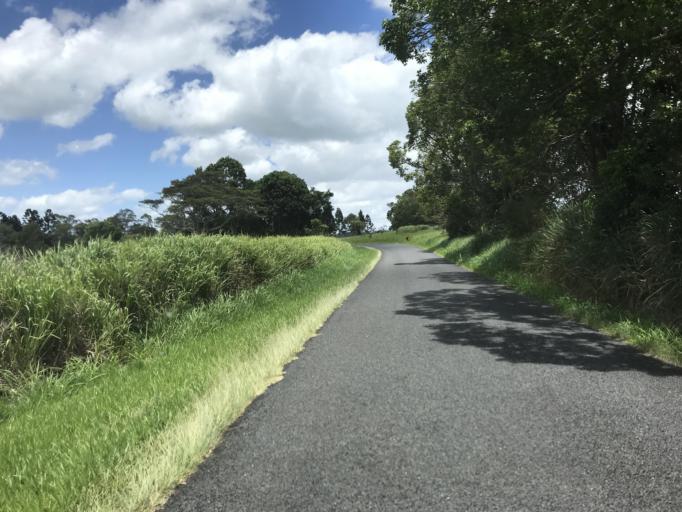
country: AU
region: Queensland
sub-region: Tablelands
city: Atherton
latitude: -17.3380
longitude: 145.5855
